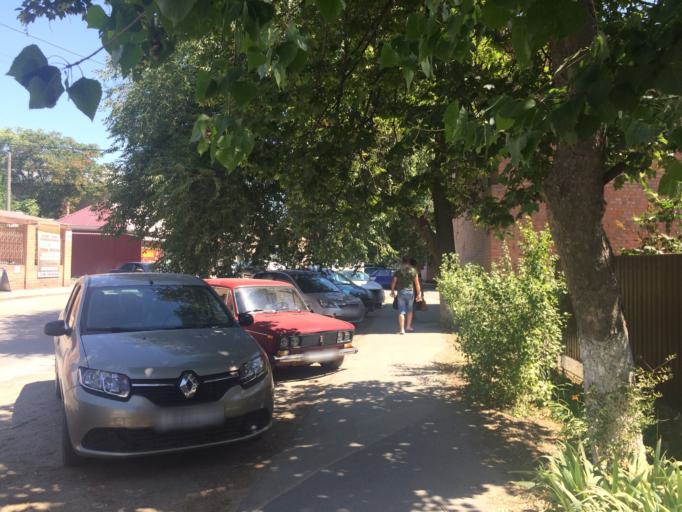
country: RU
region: Rostov
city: Sal'sk
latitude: 46.4735
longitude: 41.5375
